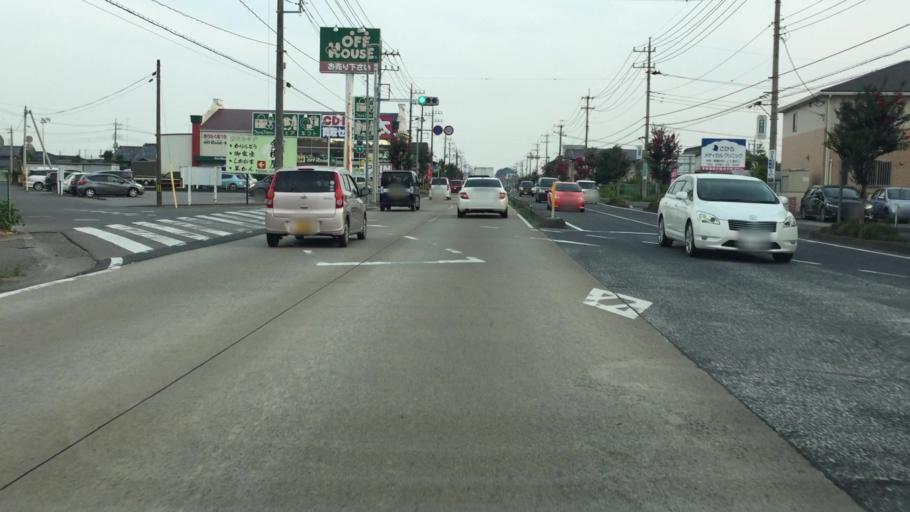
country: JP
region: Tochigi
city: Tochigi
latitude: 36.3815
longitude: 139.7164
